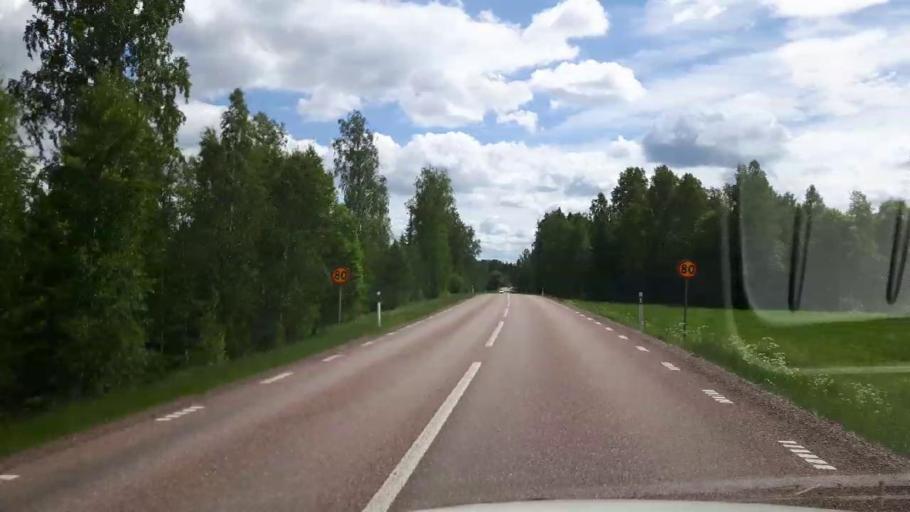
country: SE
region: Dalarna
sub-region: Saters Kommun
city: Saeter
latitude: 60.4138
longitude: 15.8507
